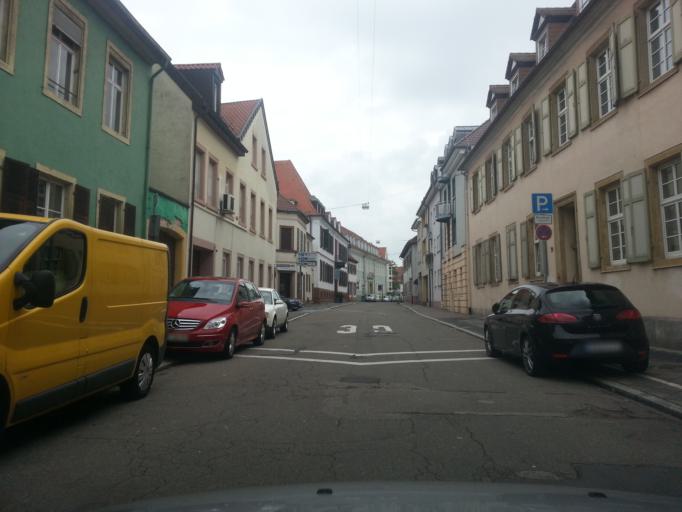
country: DE
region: Rheinland-Pfalz
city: Speyer
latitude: 49.3154
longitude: 8.4345
